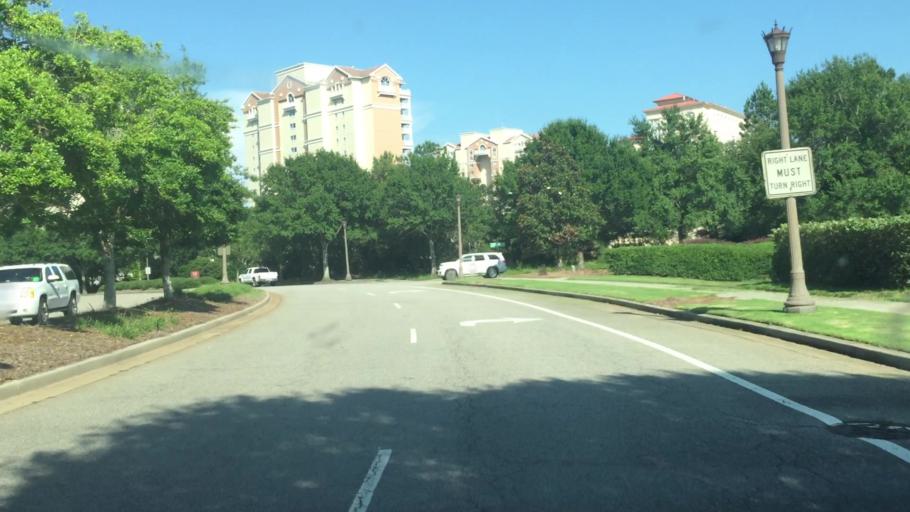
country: US
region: South Carolina
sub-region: Horry County
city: Myrtle Beach
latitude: 33.7495
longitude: -78.8111
